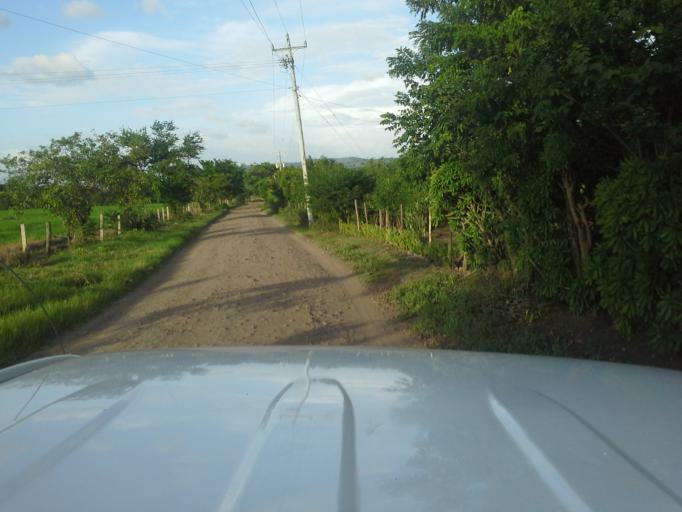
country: NI
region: Matagalpa
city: Ciudad Dario
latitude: 12.8008
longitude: -86.1435
